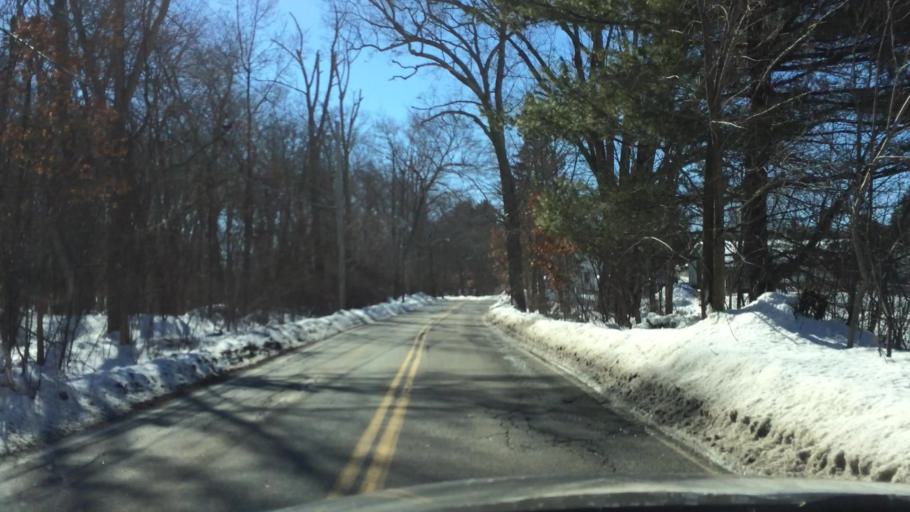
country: US
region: Massachusetts
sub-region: Middlesex County
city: Pinehurst
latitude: 42.5249
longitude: -71.2578
